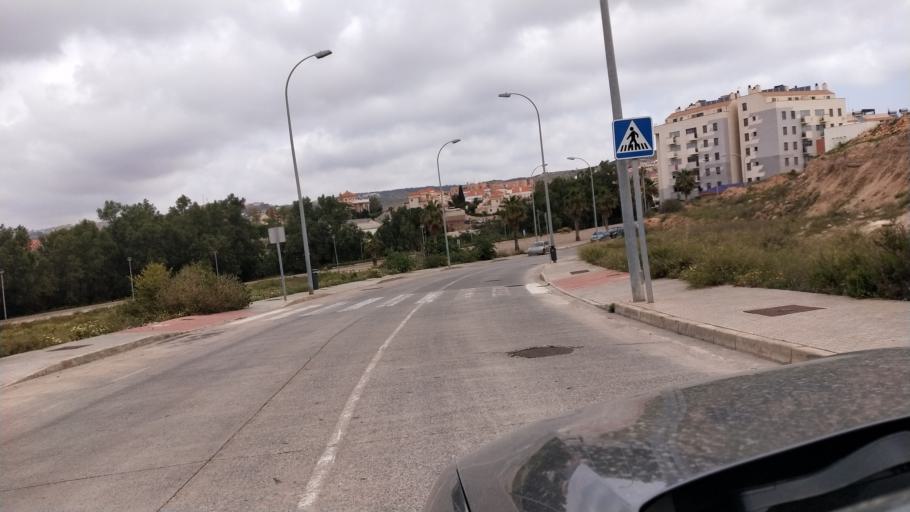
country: ES
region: Melilla
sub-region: Melilla
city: Melilla
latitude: 35.2886
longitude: -2.9567
